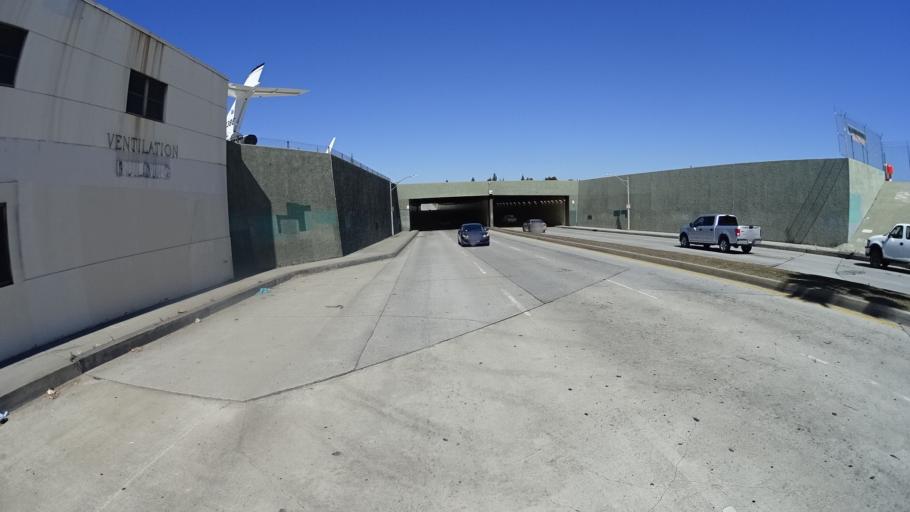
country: US
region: California
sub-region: Los Angeles County
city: Van Nuys
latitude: 34.2011
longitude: -118.4877
